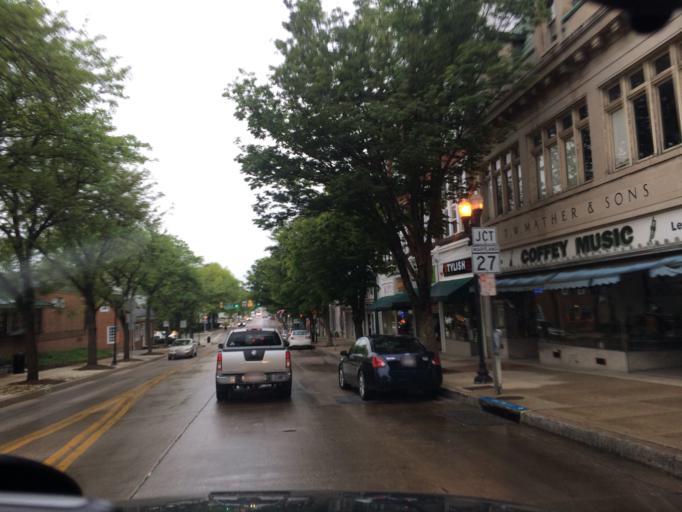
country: US
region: Maryland
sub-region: Carroll County
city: Westminster
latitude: 39.5743
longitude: -76.9950
